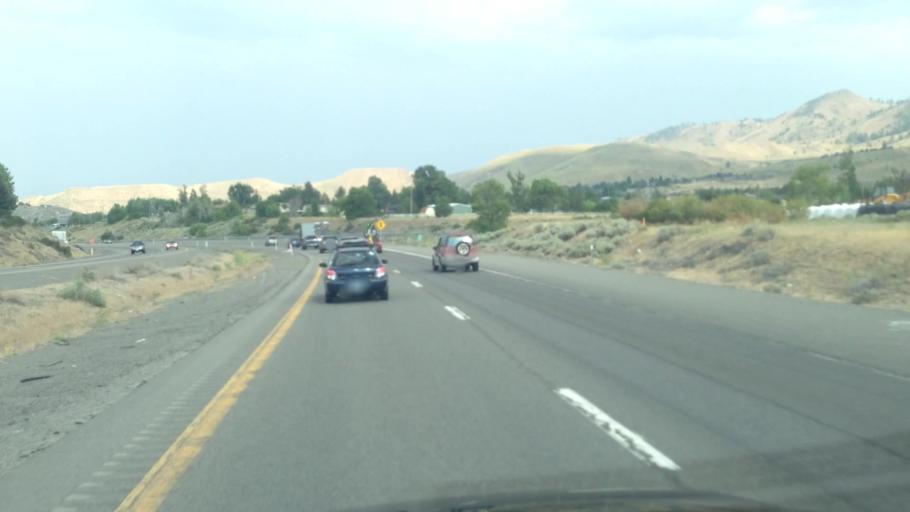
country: US
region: Nevada
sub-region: Washoe County
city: Verdi
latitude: 39.5107
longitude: -119.9638
